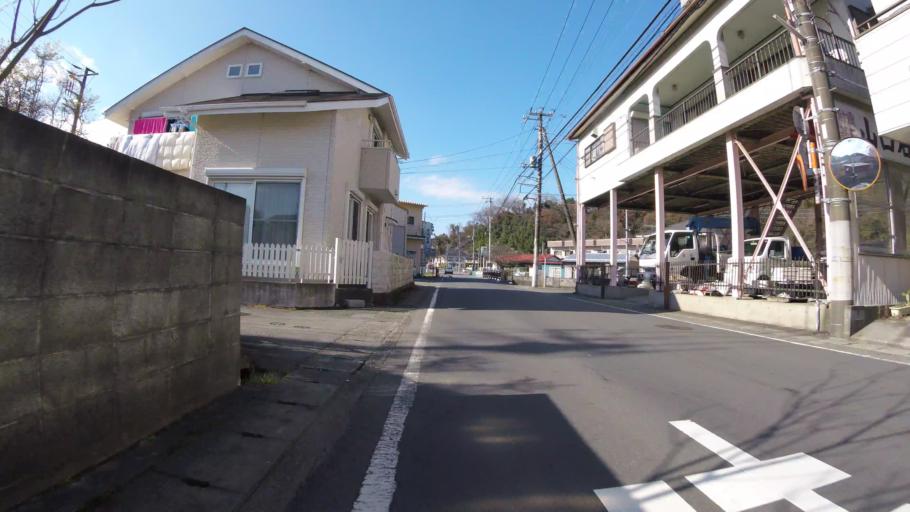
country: JP
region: Shizuoka
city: Mishima
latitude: 34.9926
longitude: 138.9444
